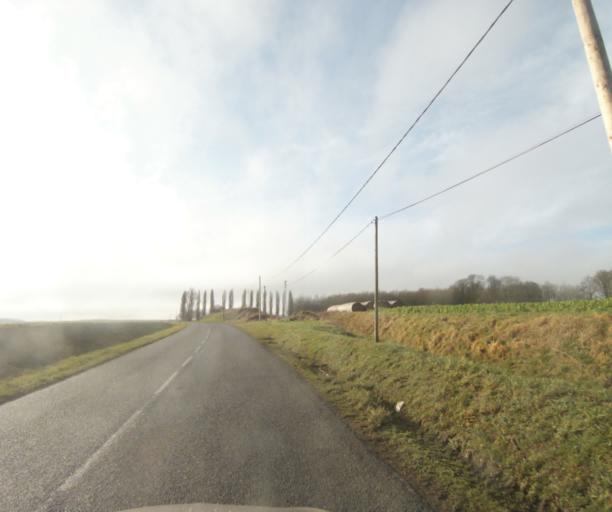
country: FR
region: Nord-Pas-de-Calais
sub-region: Departement du Nord
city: Thiant
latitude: 50.2808
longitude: 3.4414
